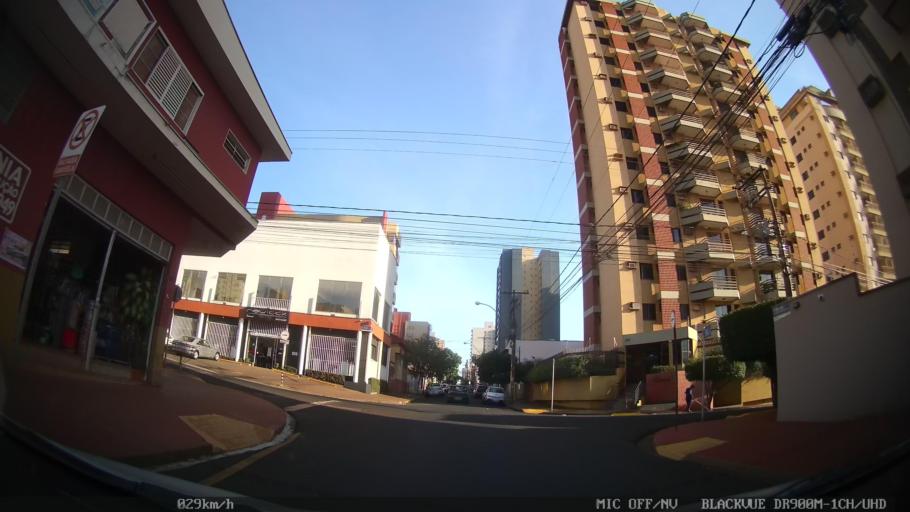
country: BR
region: Sao Paulo
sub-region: Ribeirao Preto
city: Ribeirao Preto
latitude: -21.1866
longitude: -47.8019
